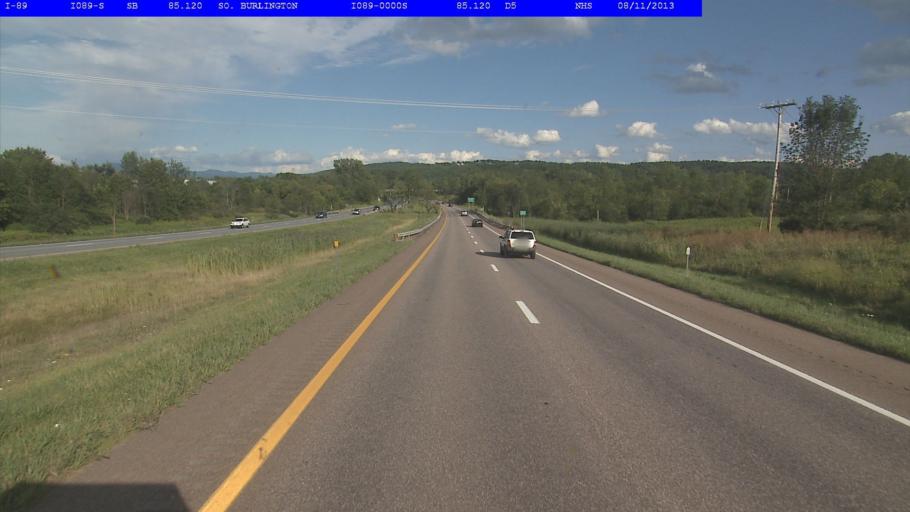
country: US
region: Vermont
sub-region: Chittenden County
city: South Burlington
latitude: 44.4430
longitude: -73.1377
